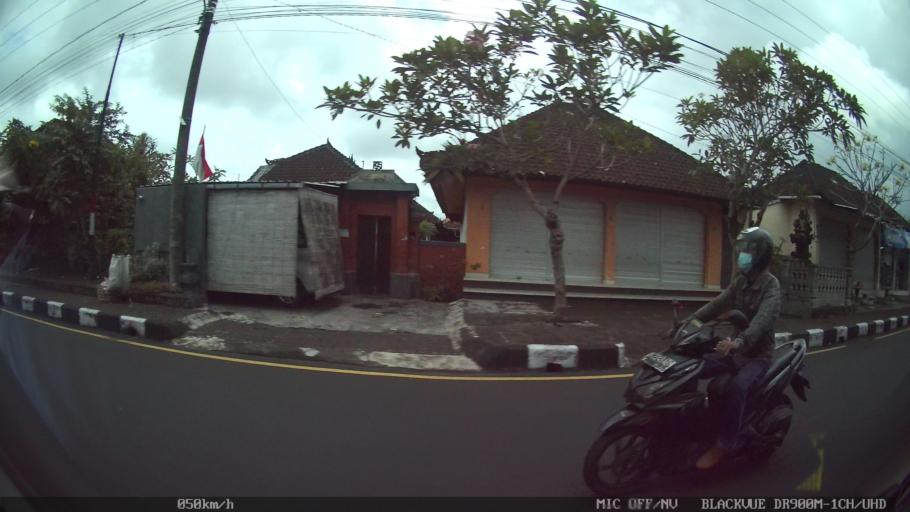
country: ID
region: Bali
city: Banjar Serangan
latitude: -8.5427
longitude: 115.1702
